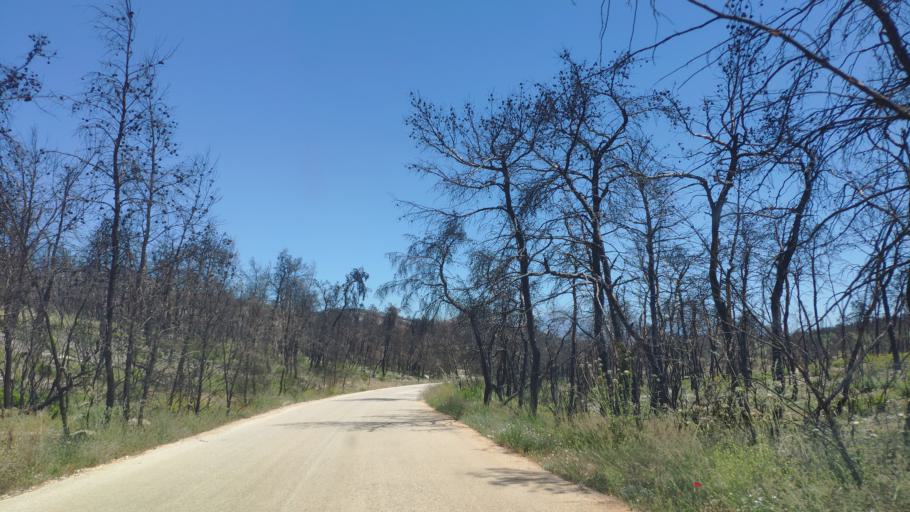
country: GR
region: Peloponnese
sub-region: Nomos Korinthias
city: Athikia
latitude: 37.8377
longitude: 22.9435
